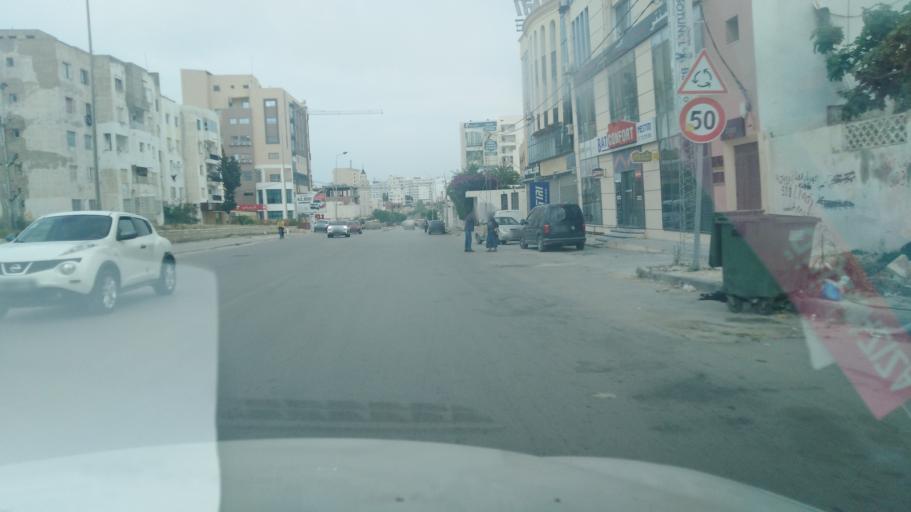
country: TN
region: Susah
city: Hammam Sousse
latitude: 35.8435
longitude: 10.6159
